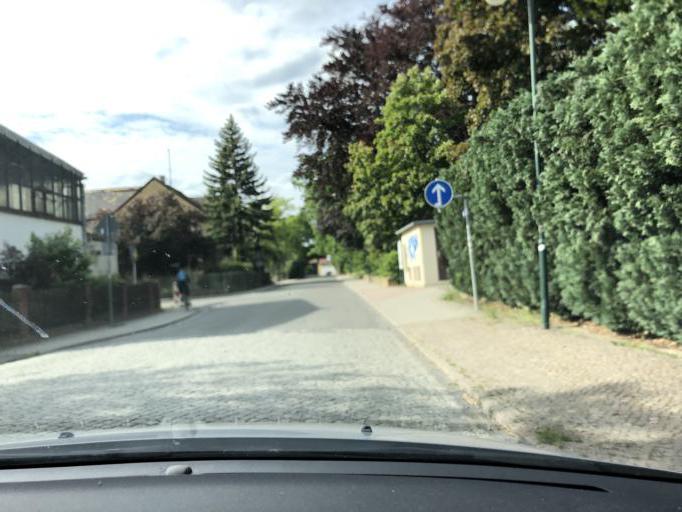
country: DE
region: Saxony
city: Brandis
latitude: 51.3296
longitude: 12.6055
